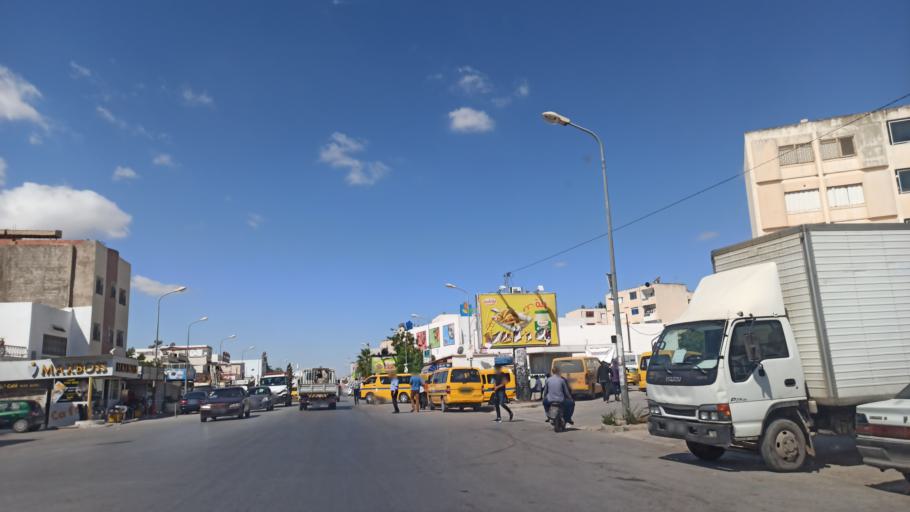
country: TN
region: Manouba
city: Manouba
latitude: 36.8014
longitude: 10.1103
